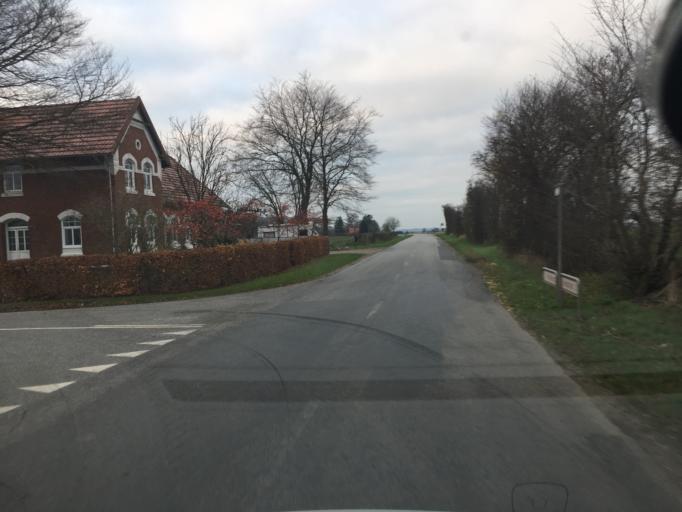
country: DK
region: South Denmark
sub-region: Tonder Kommune
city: Logumkloster
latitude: 55.0710
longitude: 9.0691
